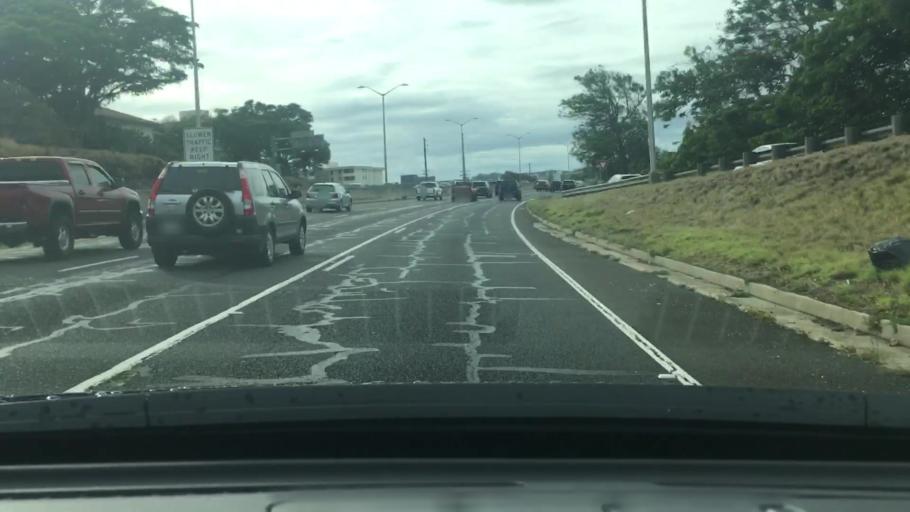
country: US
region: Hawaii
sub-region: Honolulu County
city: Honolulu
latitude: 21.2909
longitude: -157.8175
